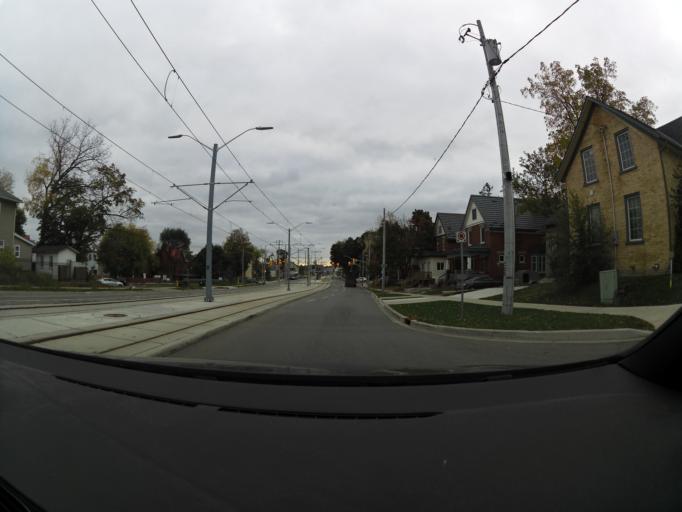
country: CA
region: Ontario
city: Kitchener
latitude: 43.4470
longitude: -80.4853
